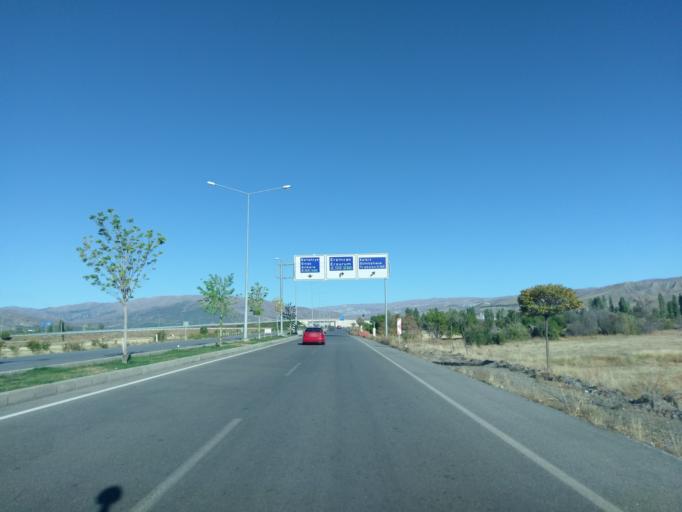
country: TR
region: Erzincan
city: Catalarmut
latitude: 39.7865
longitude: 39.3997
